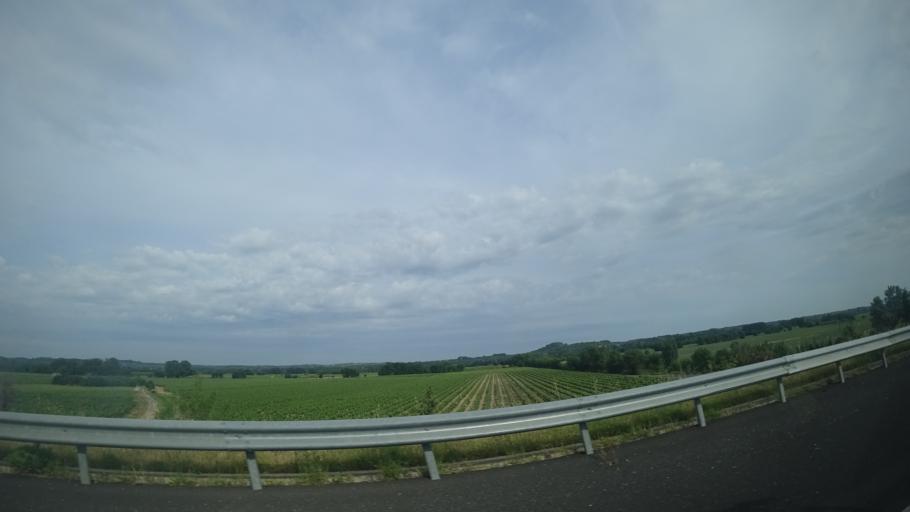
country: FR
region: Languedoc-Roussillon
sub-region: Departement de l'Herault
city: Lezignan-la-Cebe
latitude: 43.4914
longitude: 3.4454
